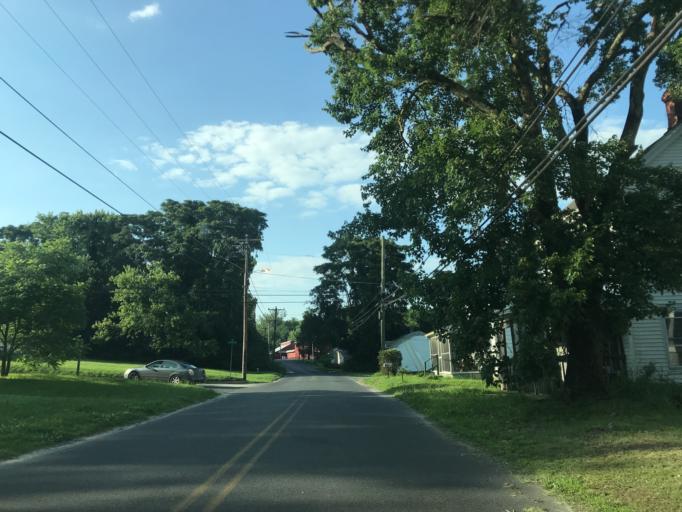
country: US
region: Maryland
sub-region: Caroline County
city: Federalsburg
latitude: 38.7004
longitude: -75.7759
